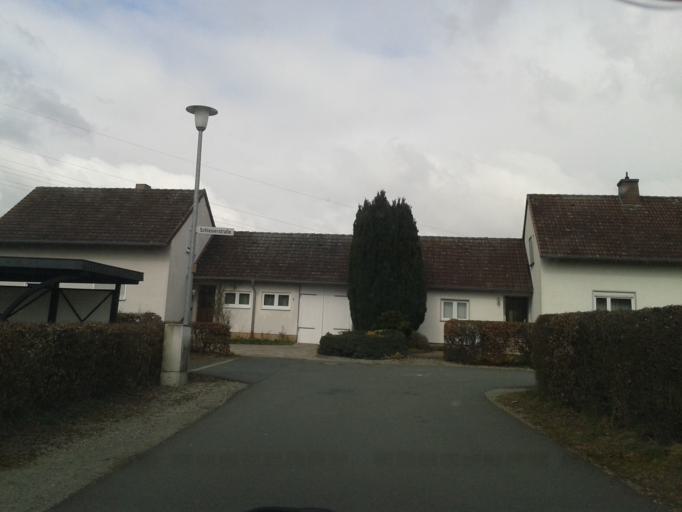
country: DE
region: North Rhine-Westphalia
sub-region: Regierungsbezirk Detmold
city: Schieder-Schwalenberg
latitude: 51.9253
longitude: 9.1526
